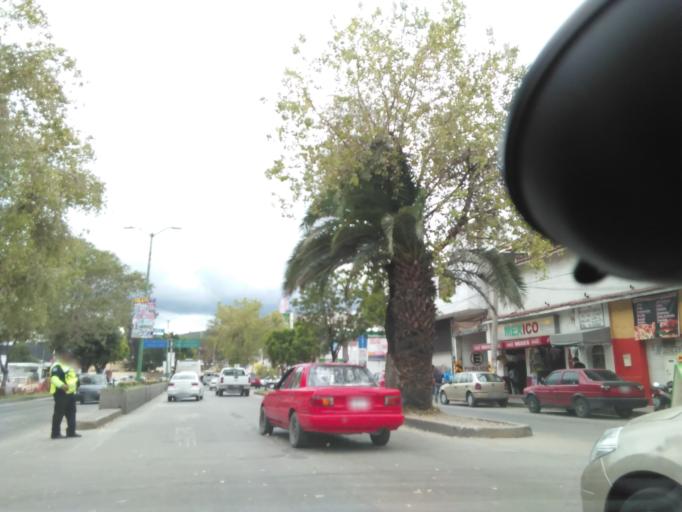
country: MX
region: Hidalgo
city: Tula de Allende
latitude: 20.0545
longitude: -99.3390
